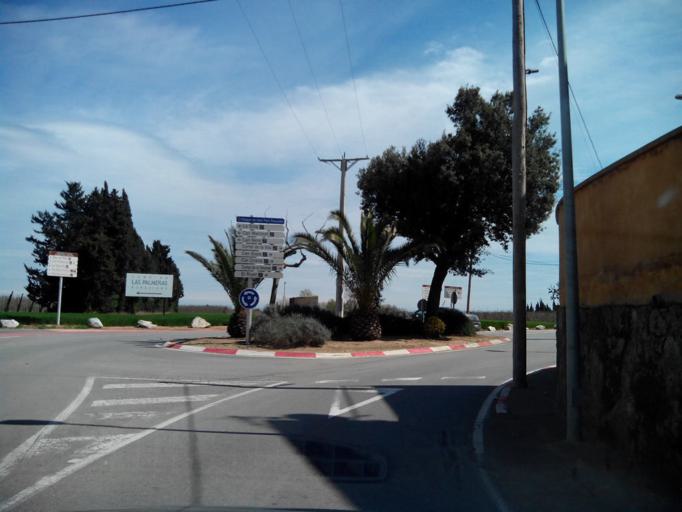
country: ES
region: Catalonia
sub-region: Provincia de Girona
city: Sant Pere Pescador
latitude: 42.1864
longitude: 3.0913
